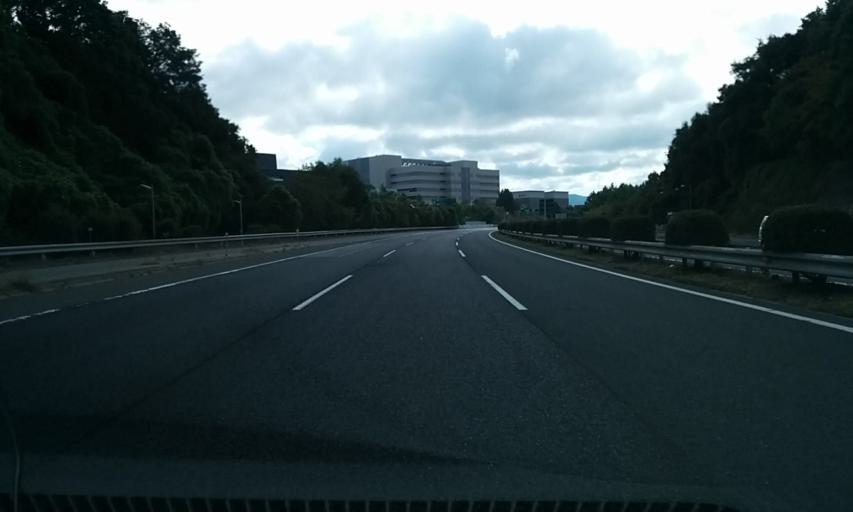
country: JP
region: Hyogo
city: Sandacho
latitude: 34.8655
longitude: 135.2106
